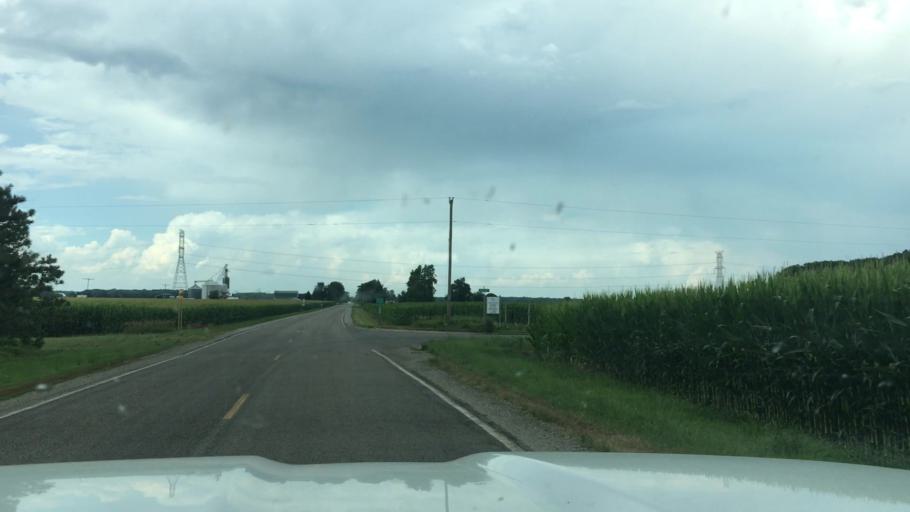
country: US
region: Michigan
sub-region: Montcalm County
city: Carson City
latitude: 43.2048
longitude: -84.7779
